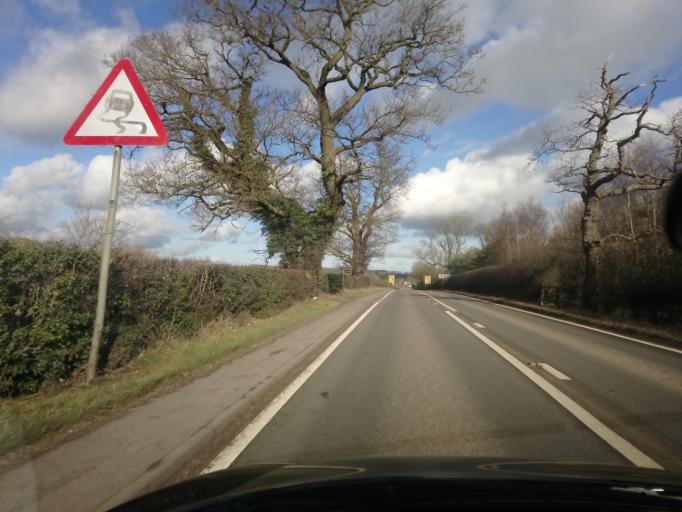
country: GB
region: England
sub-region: Shropshire
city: Astley
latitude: 52.7661
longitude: -2.7150
